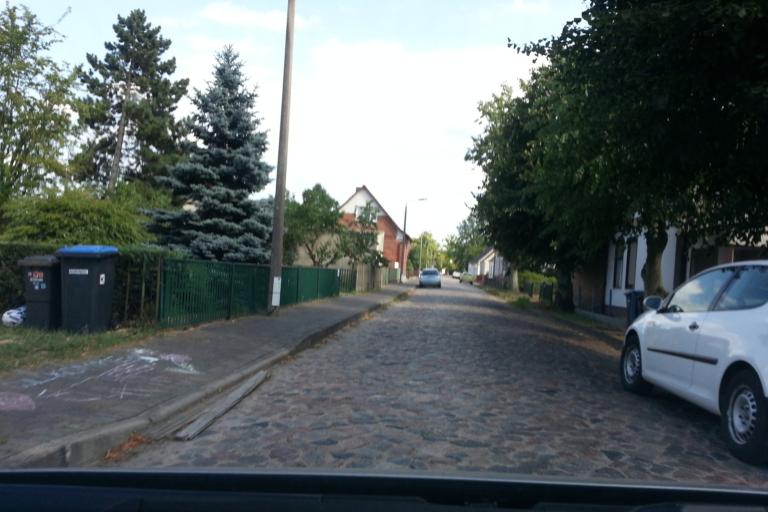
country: DE
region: Mecklenburg-Vorpommern
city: Ferdinandshof
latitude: 53.6312
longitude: 13.8585
